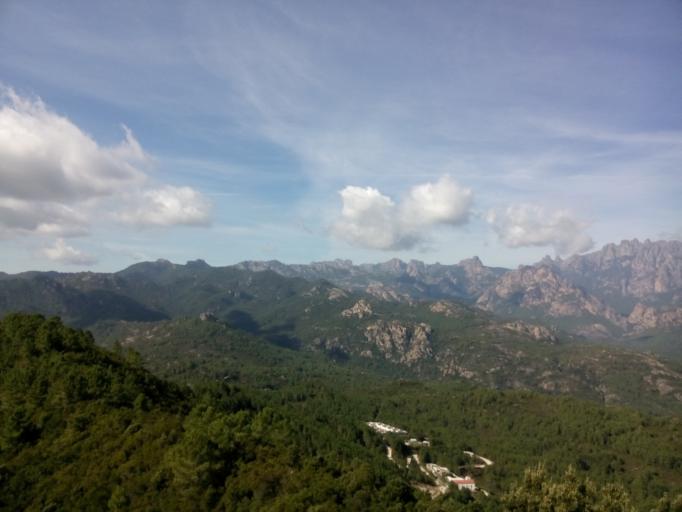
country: FR
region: Corsica
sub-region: Departement de la Corse-du-Sud
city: Sari-Solenzara
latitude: 41.8264
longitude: 9.3620
